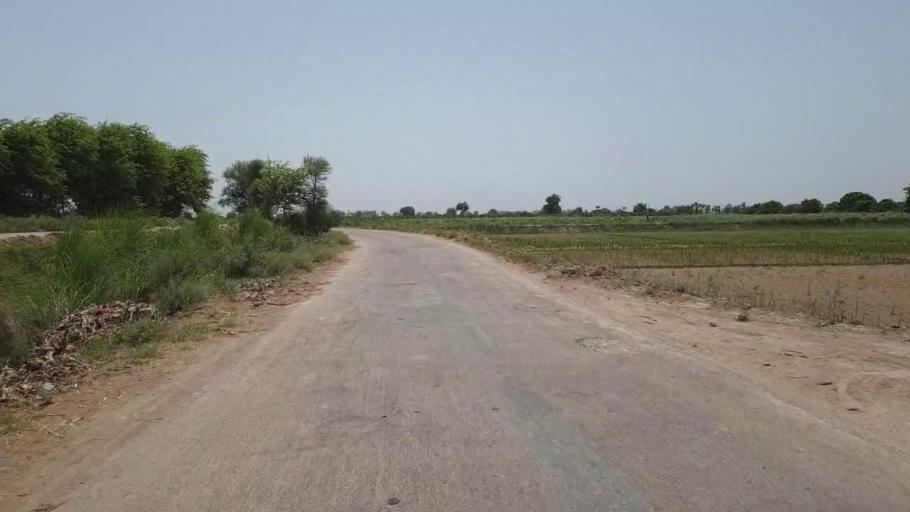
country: PK
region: Sindh
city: Daur
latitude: 26.3853
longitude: 68.1811
